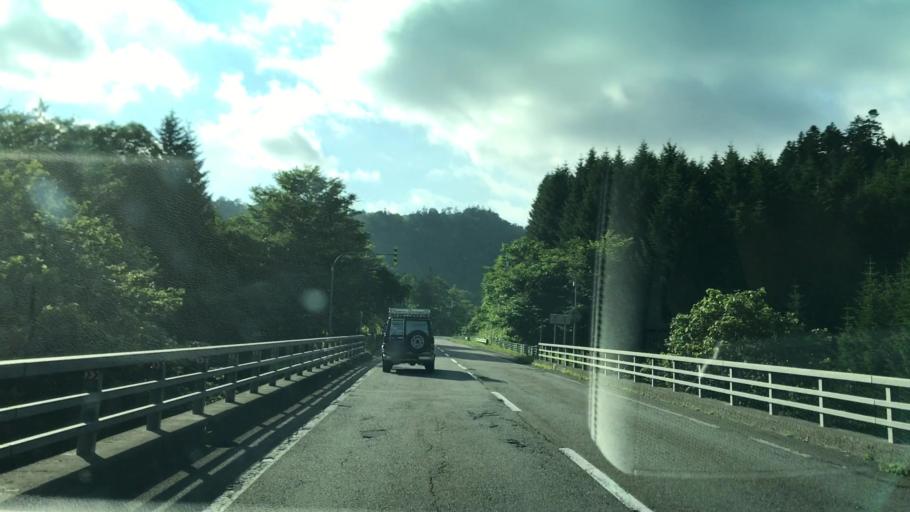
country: JP
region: Hokkaido
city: Iwamizawa
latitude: 42.9089
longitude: 142.1249
